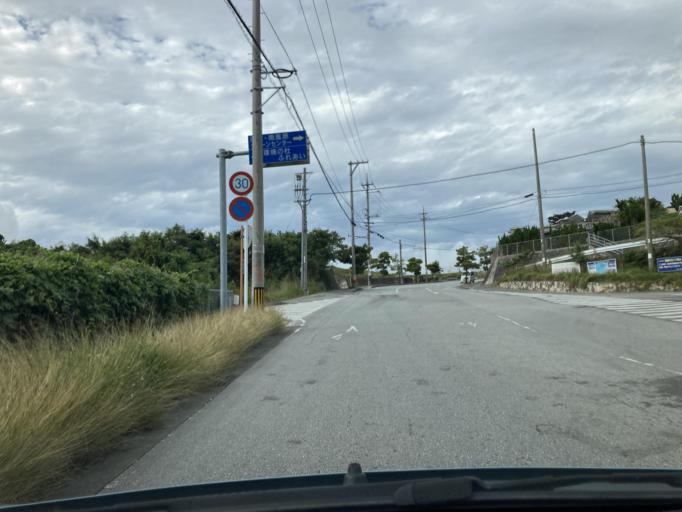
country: JP
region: Okinawa
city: Naha-shi
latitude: 26.2135
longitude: 127.7304
